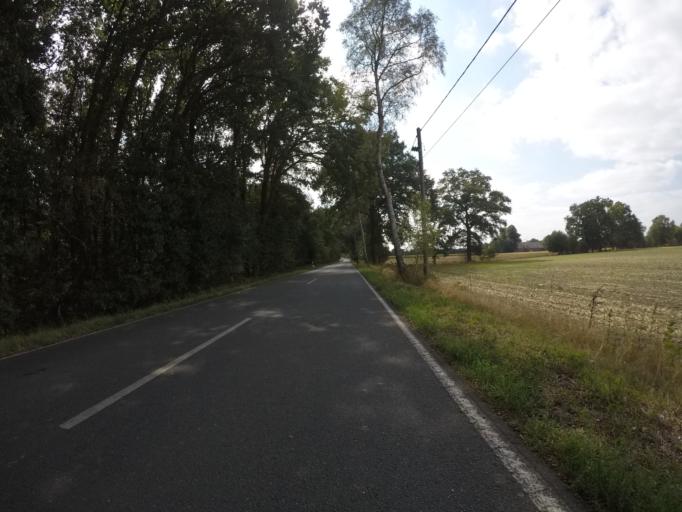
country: DE
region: North Rhine-Westphalia
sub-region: Regierungsbezirk Munster
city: Isselburg
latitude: 51.8113
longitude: 6.4779
